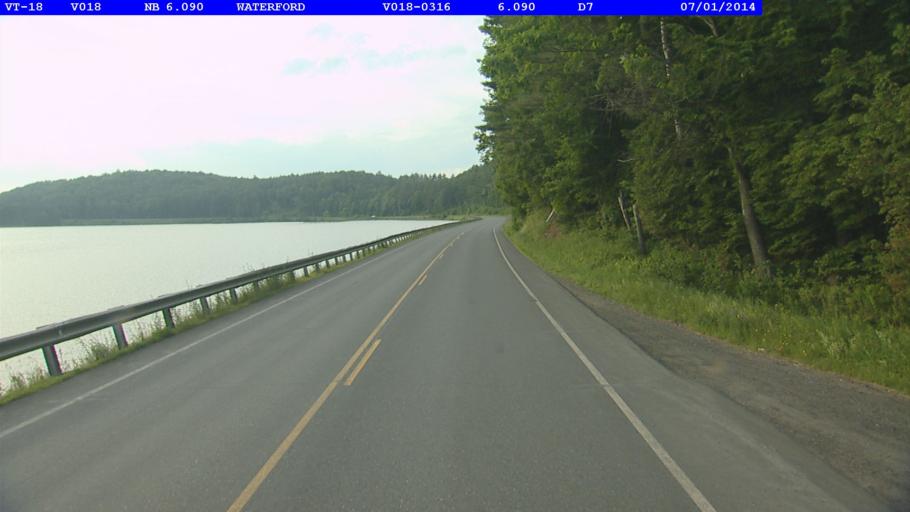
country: US
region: Vermont
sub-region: Caledonia County
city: Saint Johnsbury
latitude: 44.4159
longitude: -71.9369
